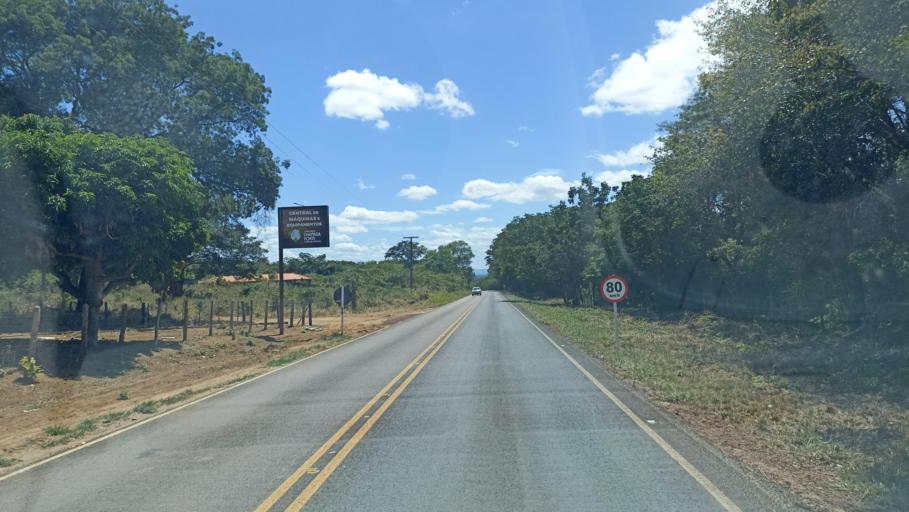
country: BR
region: Bahia
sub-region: Andarai
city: Vera Cruz
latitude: -12.7883
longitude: -41.3286
